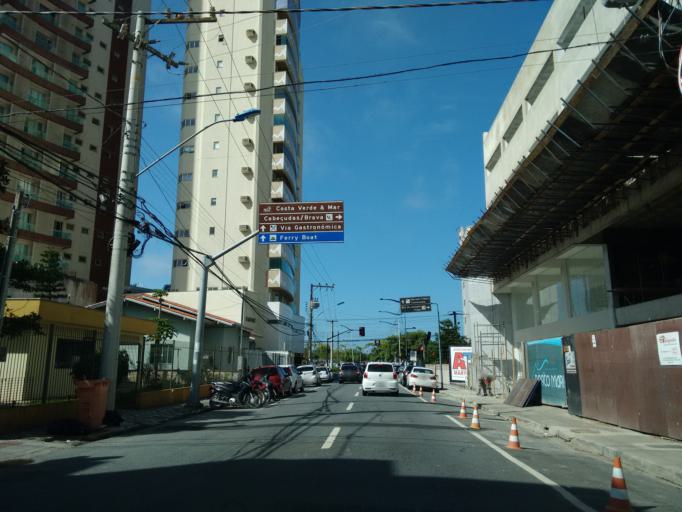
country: BR
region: Santa Catarina
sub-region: Itajai
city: Itajai
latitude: -26.9205
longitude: -48.6506
